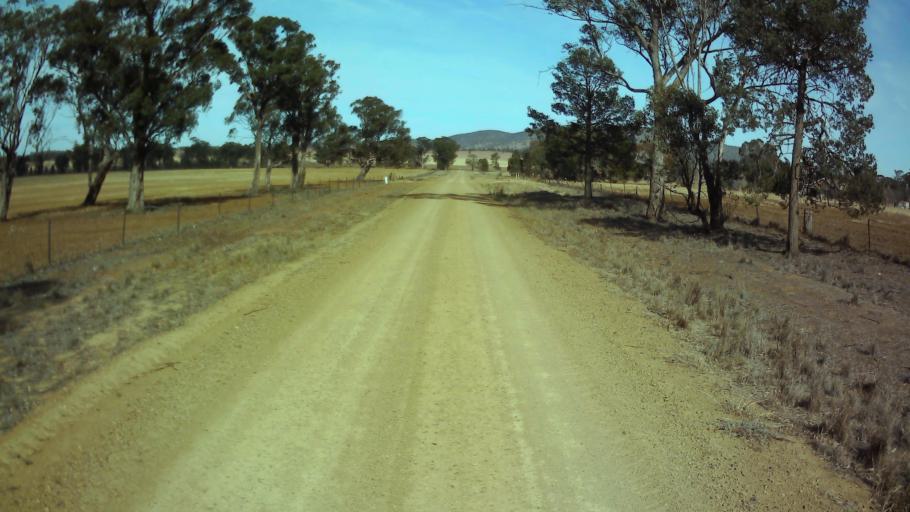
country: AU
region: New South Wales
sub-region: Weddin
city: Grenfell
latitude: -33.7510
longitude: 147.9964
